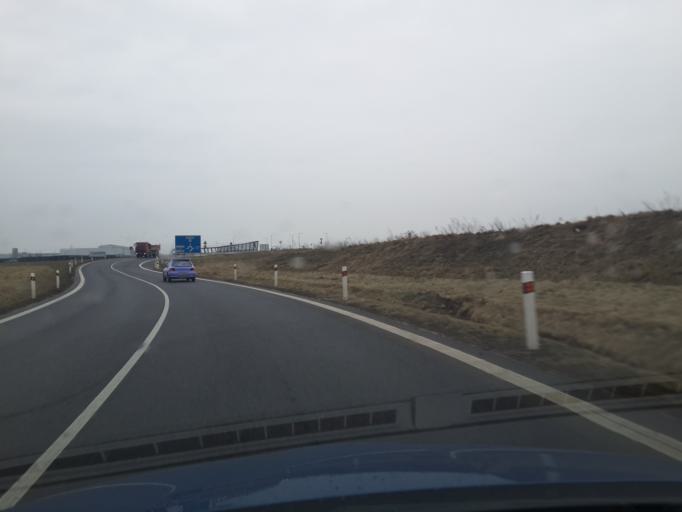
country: SK
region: Bratislavsky
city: Stupava
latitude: 48.2458
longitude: 16.9913
